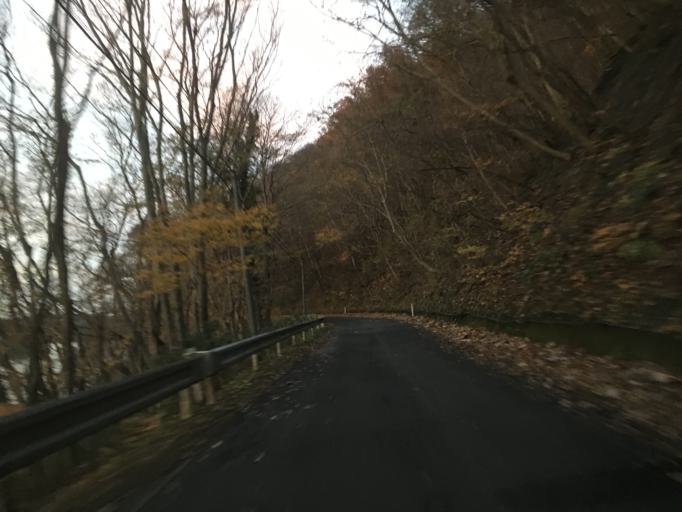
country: JP
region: Iwate
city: Ichinoseki
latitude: 38.8123
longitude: 141.2522
